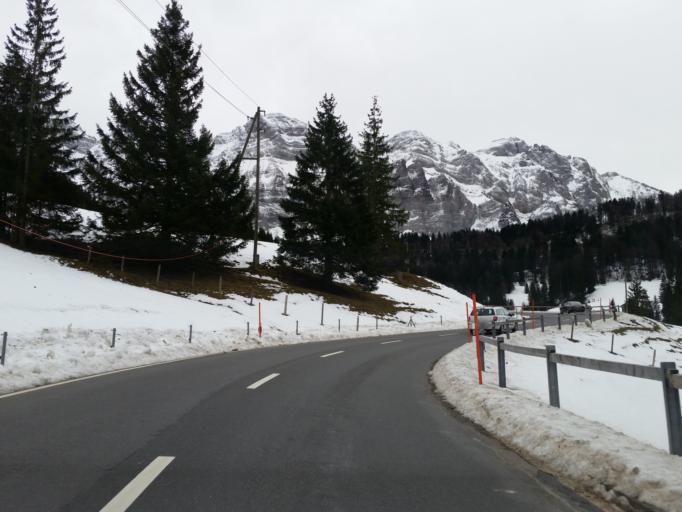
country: CH
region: Appenzell Ausserrhoden
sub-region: Bezirk Hinterland
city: Urnasch
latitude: 47.2641
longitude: 9.2968
